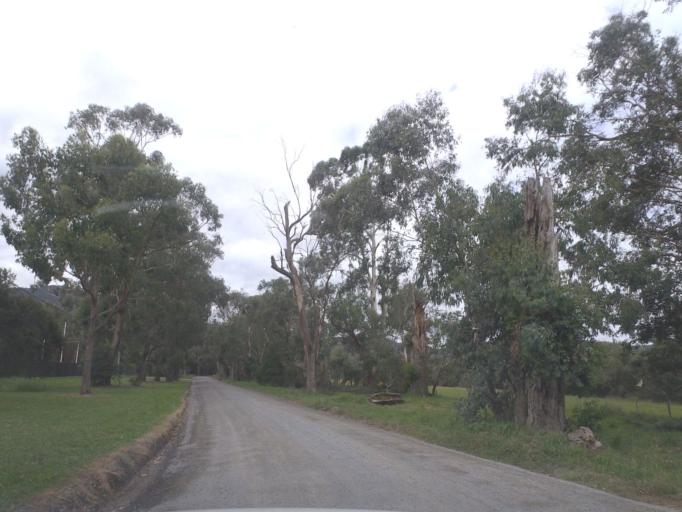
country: AU
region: Victoria
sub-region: Knox
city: The Basin
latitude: -37.8447
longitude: 145.3178
